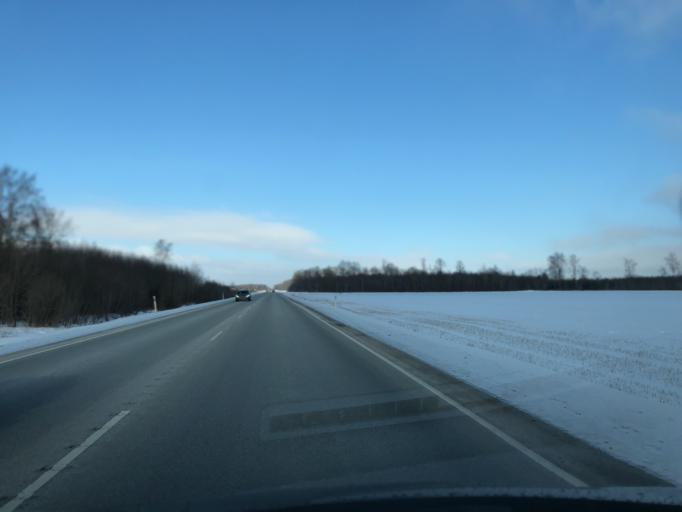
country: EE
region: Jaervamaa
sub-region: Paide linn
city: Paide
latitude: 58.7899
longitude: 25.7582
